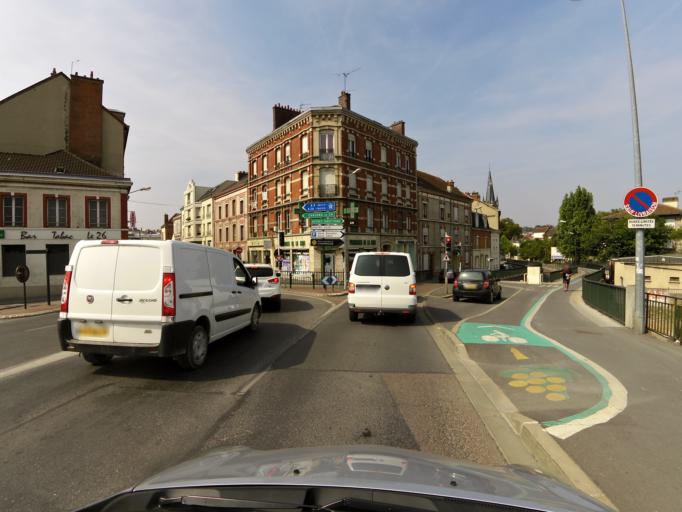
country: FR
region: Champagne-Ardenne
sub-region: Departement de la Marne
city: Magenta
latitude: 49.0457
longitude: 3.9620
